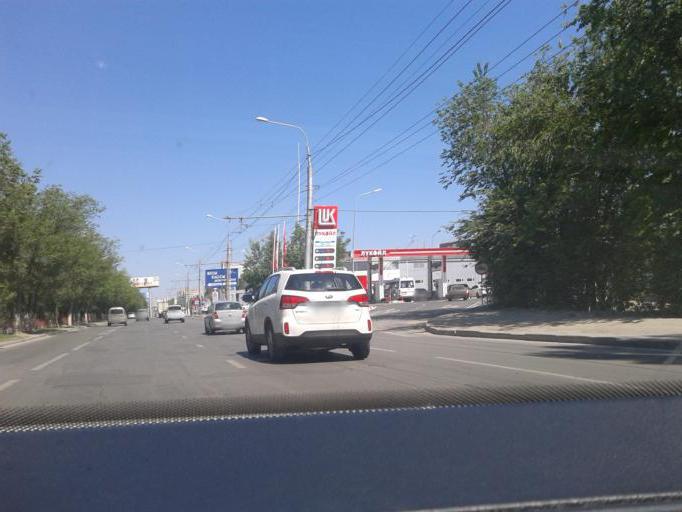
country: RU
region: Volgograd
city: Volgograd
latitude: 48.7386
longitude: 44.4926
